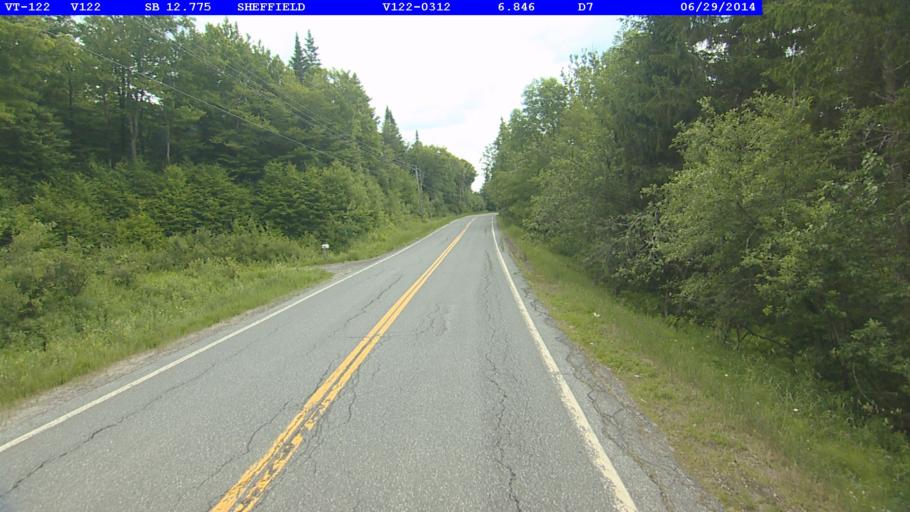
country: US
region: Vermont
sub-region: Caledonia County
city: Lyndonville
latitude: 44.6668
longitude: -72.1609
